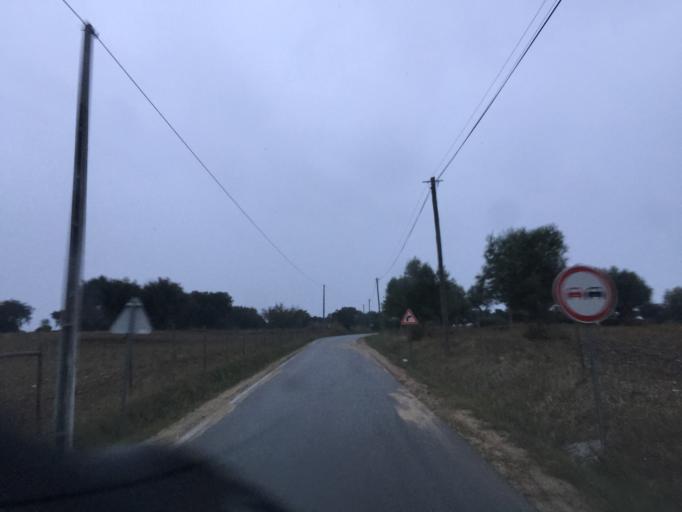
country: PT
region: Portalegre
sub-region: Avis
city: Avis
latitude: 39.0521
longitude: -7.9012
